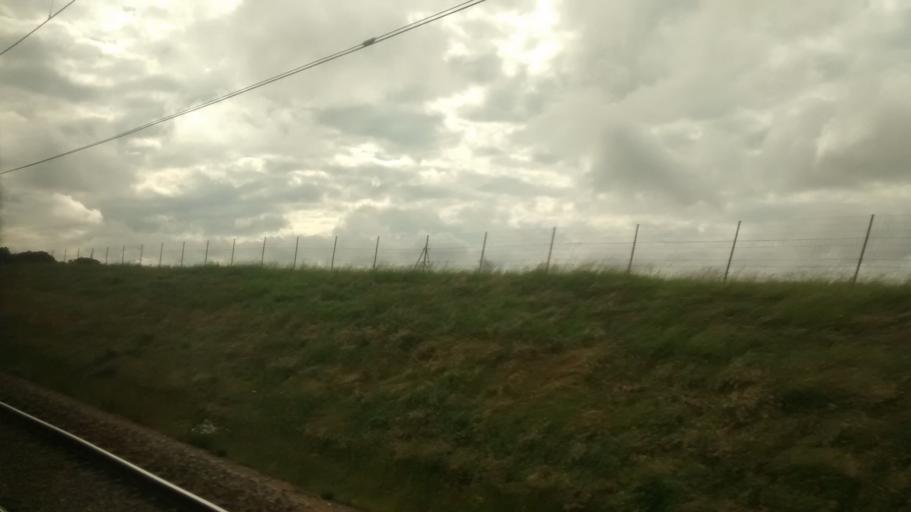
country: FR
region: Centre
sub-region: Departement d'Eure-et-Loir
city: Bonneval
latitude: 48.1868
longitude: 1.3188
